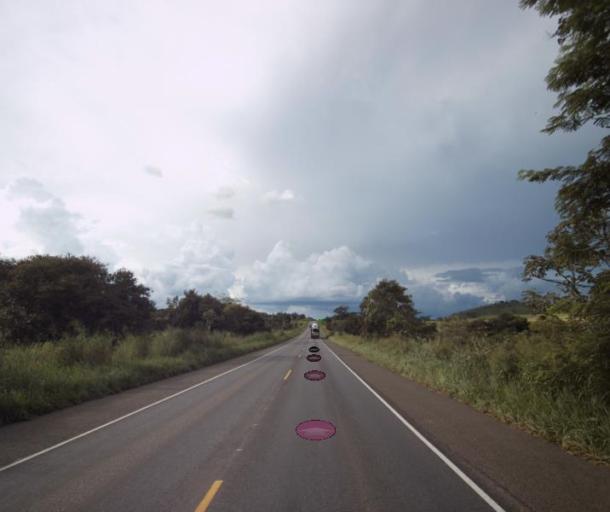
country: BR
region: Goias
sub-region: Ceres
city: Ceres
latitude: -15.2332
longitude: -49.5553
